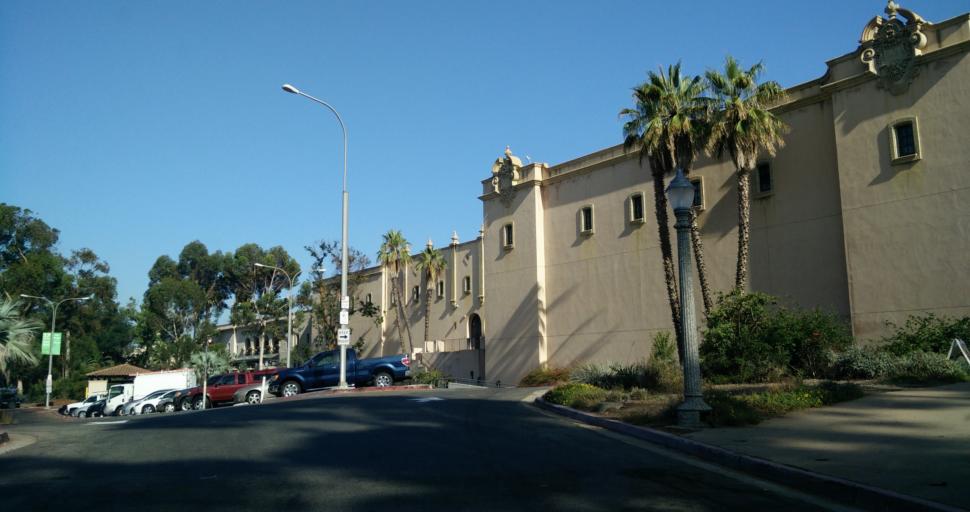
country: US
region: California
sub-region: San Diego County
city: San Diego
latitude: 32.7304
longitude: -117.1480
